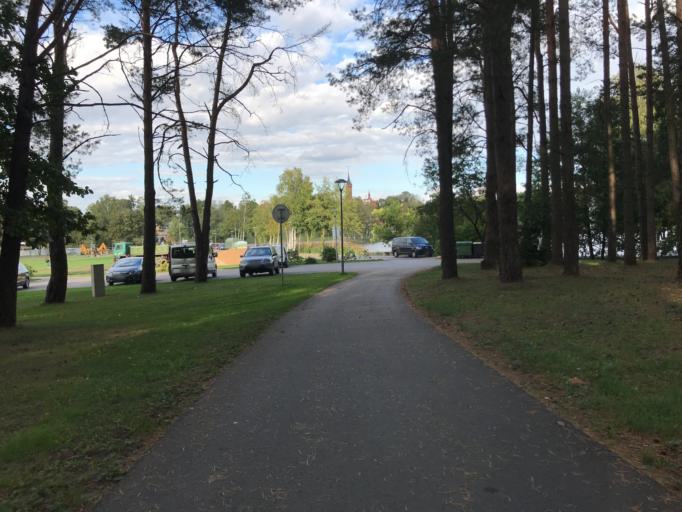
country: LT
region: Alytaus apskritis
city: Druskininkai
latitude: 54.0147
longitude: 23.9691
